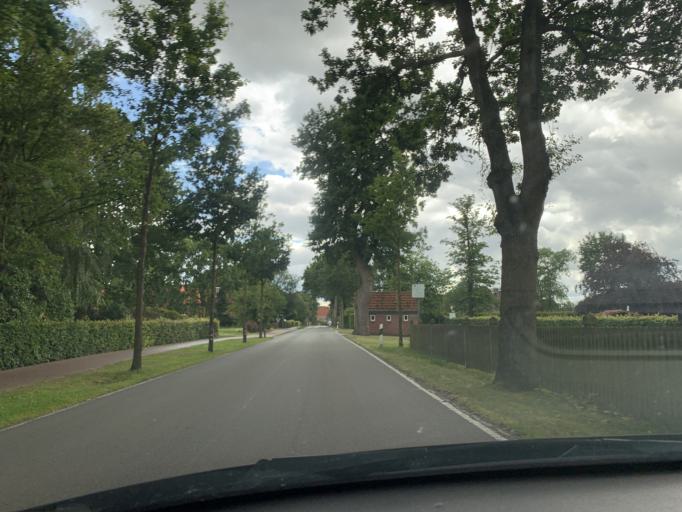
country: DE
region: Lower Saxony
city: Westerstede
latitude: 53.2134
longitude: 7.9333
